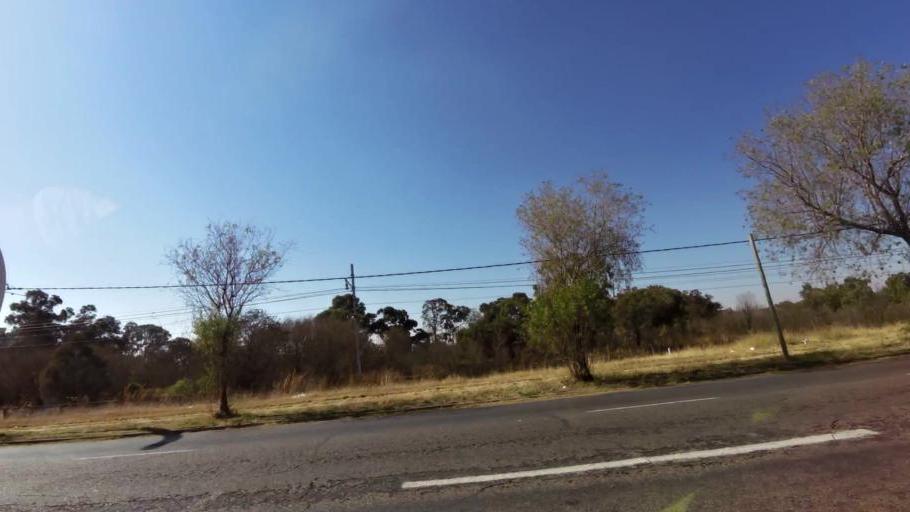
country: ZA
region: Gauteng
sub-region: City of Johannesburg Metropolitan Municipality
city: Johannesburg
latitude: -26.2347
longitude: 27.9855
